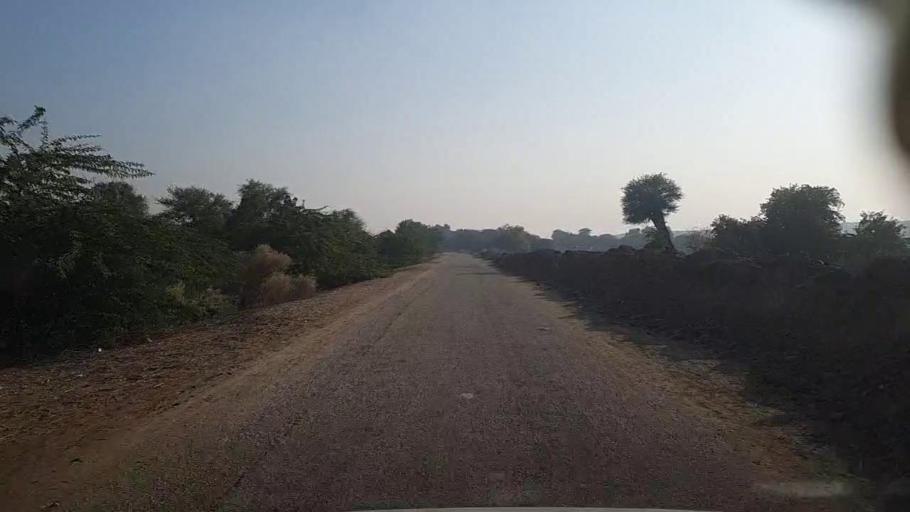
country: PK
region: Sindh
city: Karaundi
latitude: 26.7448
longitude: 68.4769
